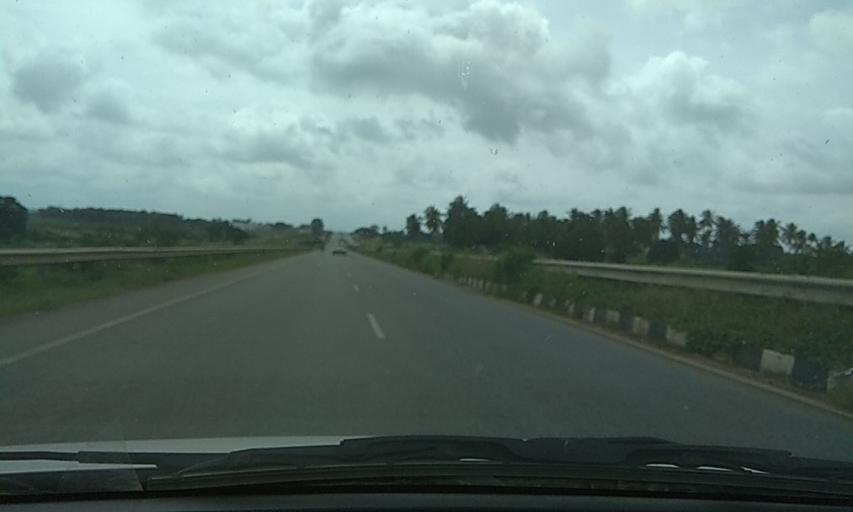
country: IN
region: Karnataka
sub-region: Davanagere
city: Harihar
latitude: 14.4583
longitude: 75.8608
